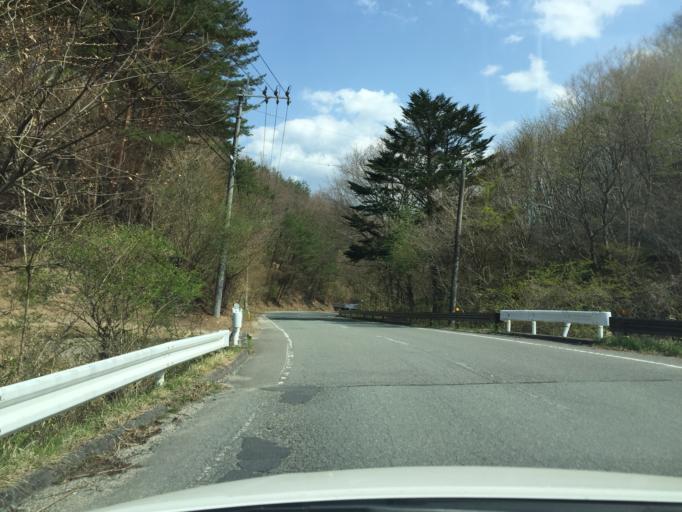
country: JP
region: Fukushima
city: Namie
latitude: 37.3644
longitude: 140.8096
